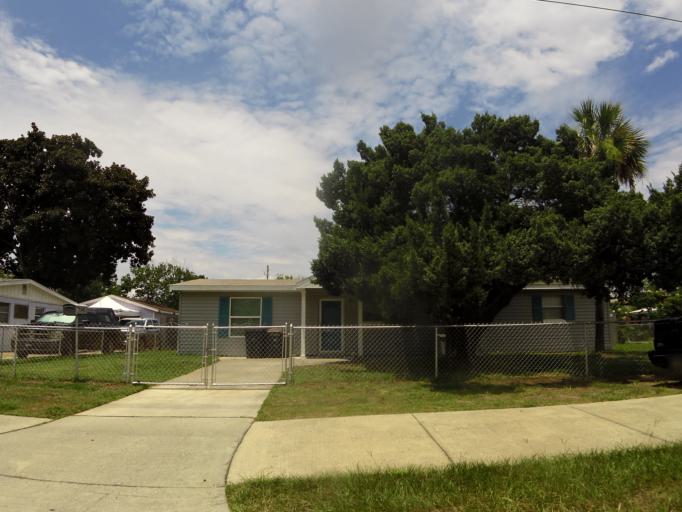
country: US
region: Florida
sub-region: Duval County
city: Atlantic Beach
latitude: 30.3330
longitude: -81.4127
